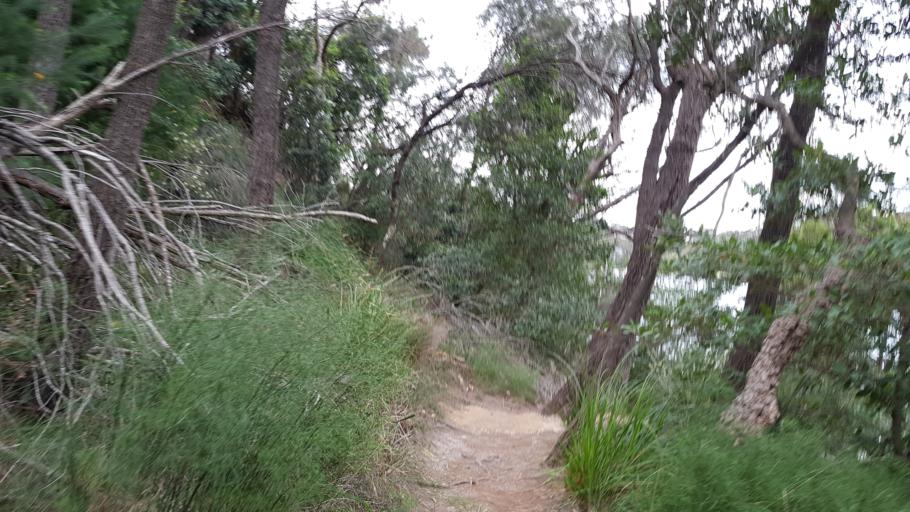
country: AU
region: New South Wales
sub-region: Willoughby
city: Castlecrag
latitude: -33.7965
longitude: 151.2211
